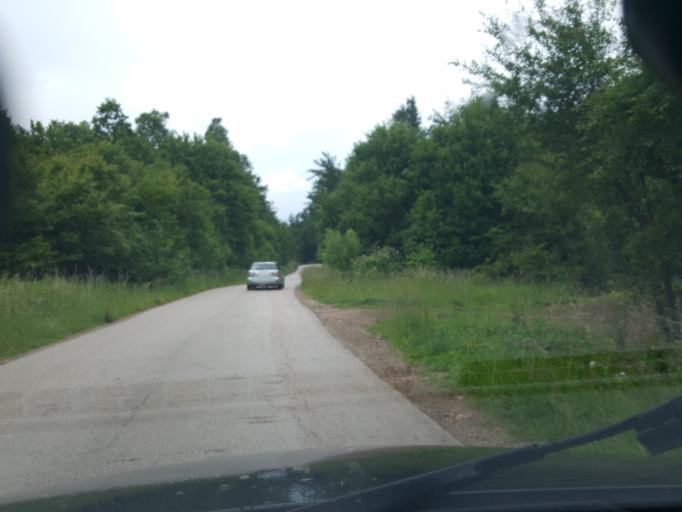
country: RS
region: Central Serbia
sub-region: Zajecarski Okrug
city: Boljevac
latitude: 43.7788
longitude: 21.9273
